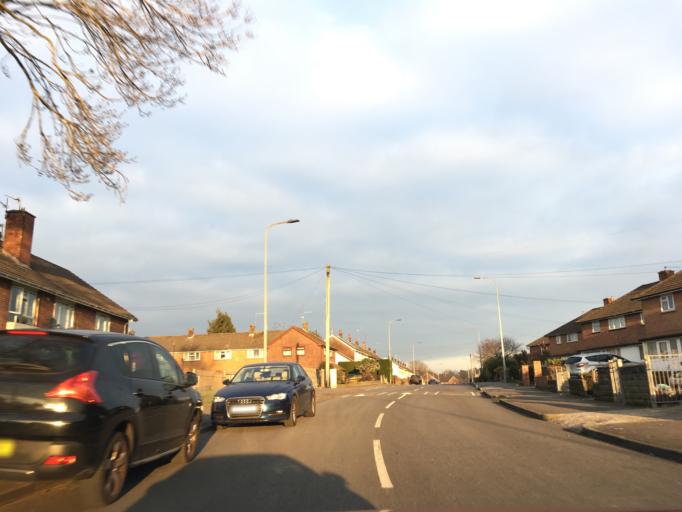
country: GB
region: Wales
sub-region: Newport
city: Marshfield
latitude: 51.5280
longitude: -3.1236
